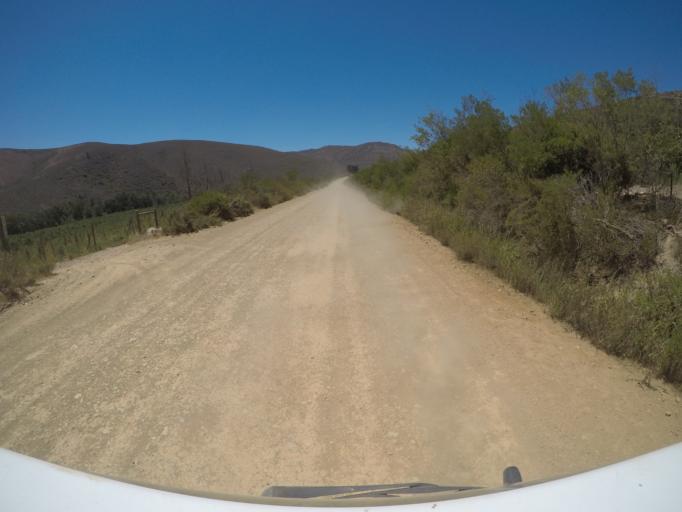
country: ZA
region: Western Cape
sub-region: Overberg District Municipality
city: Grabouw
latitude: -34.1137
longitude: 19.2278
